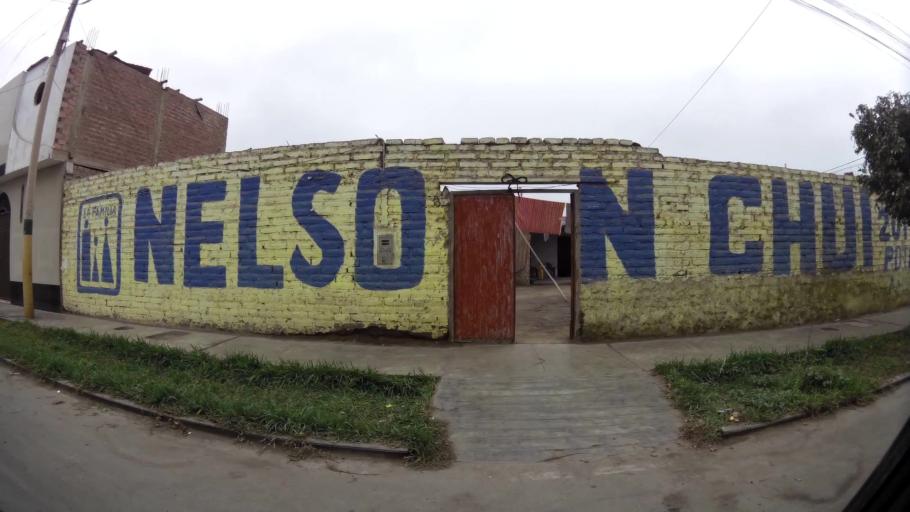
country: PE
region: Lima
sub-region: Barranca
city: Barranca
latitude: -10.7463
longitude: -77.7526
